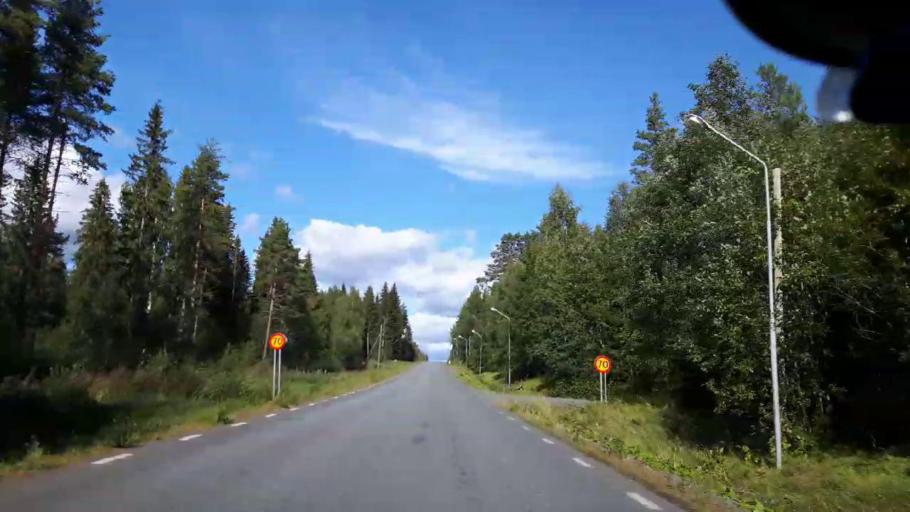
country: SE
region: Jaemtland
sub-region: Braecke Kommun
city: Braecke
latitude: 63.1817
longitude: 15.5552
